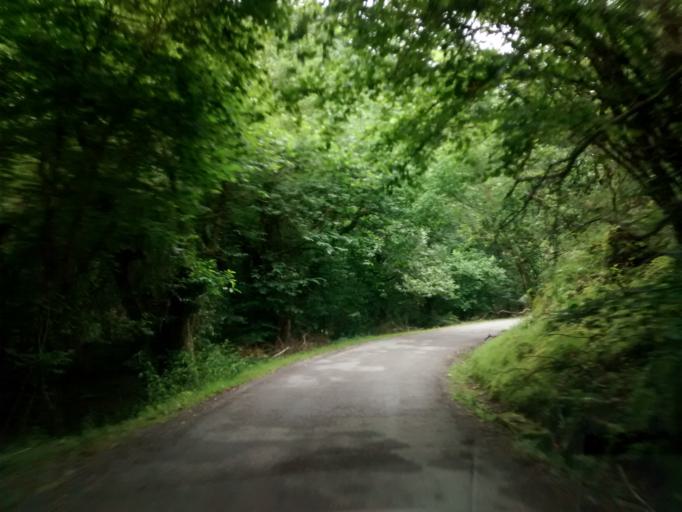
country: ES
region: Asturias
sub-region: Province of Asturias
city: Pilona
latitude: 43.2706
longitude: -5.3415
